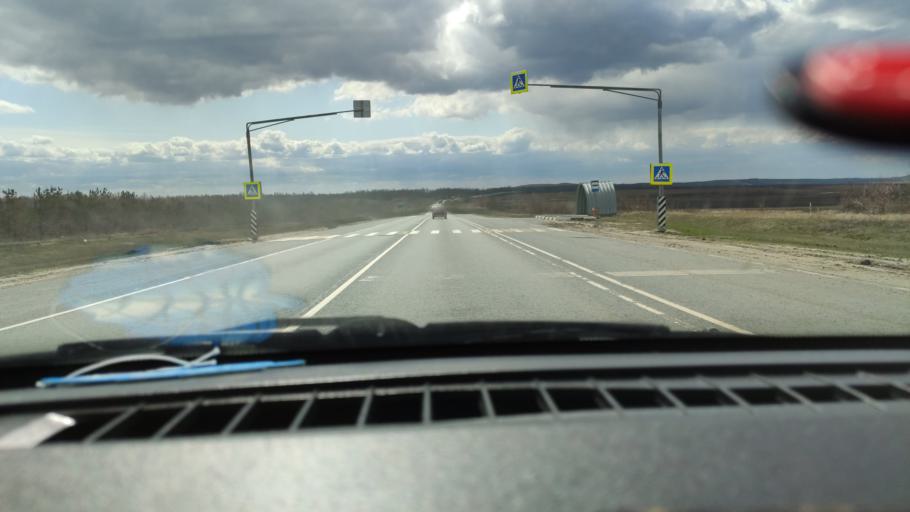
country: RU
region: Saratov
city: Alekseyevka
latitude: 52.2846
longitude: 47.9310
